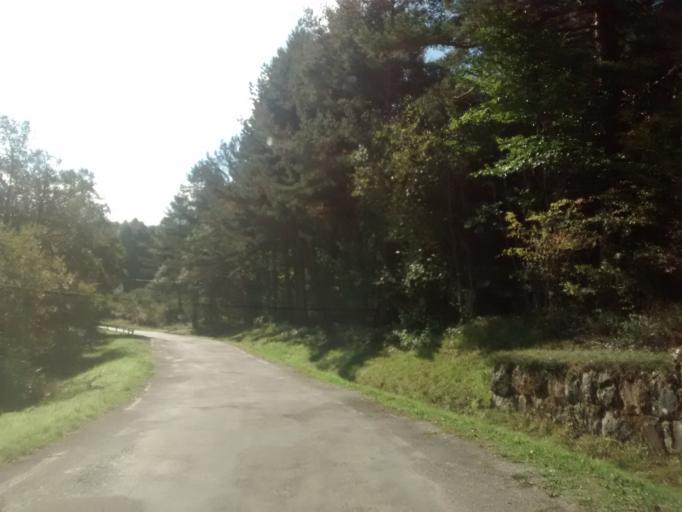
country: ES
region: Cantabria
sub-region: Provincia de Cantabria
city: Reinosa
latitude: 42.9383
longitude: -4.0494
